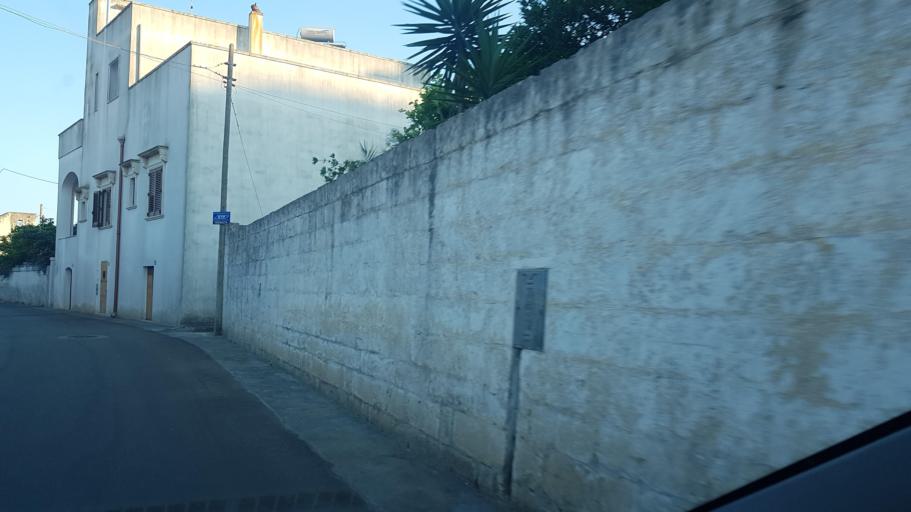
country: IT
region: Apulia
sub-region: Provincia di Lecce
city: Specchia
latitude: 39.9372
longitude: 18.3030
